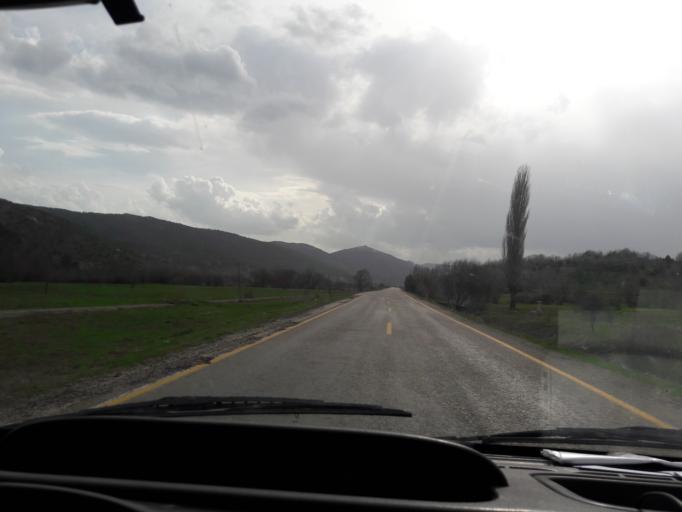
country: TR
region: Giresun
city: Alucra
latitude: 40.2668
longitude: 38.9302
